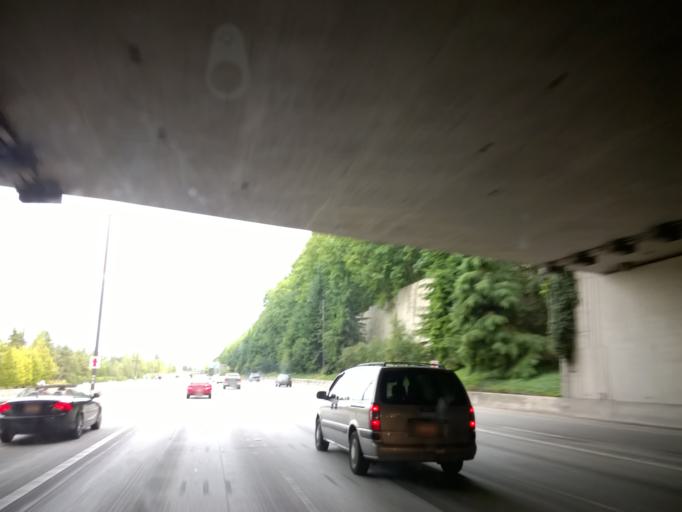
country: US
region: Washington
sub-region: King County
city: Mercer Island
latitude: 47.5848
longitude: -122.2259
